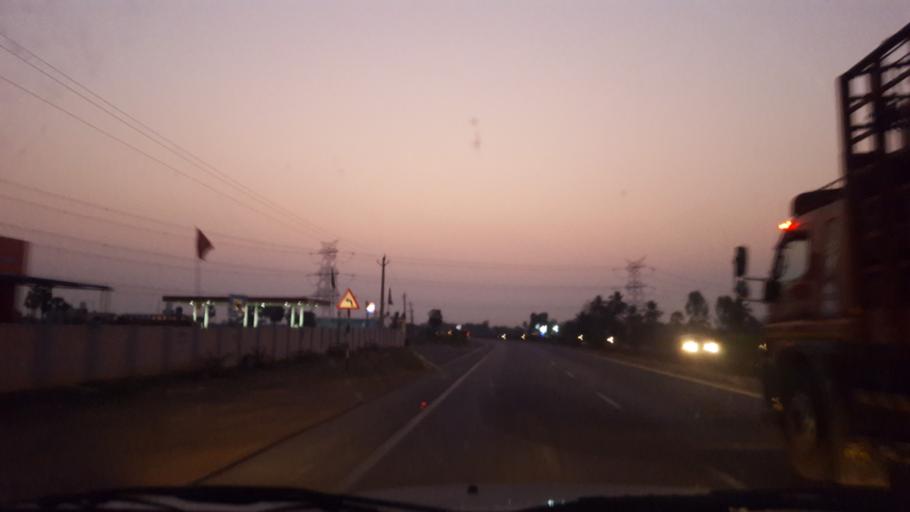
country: IN
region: Andhra Pradesh
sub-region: East Godavari
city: Peddapuram
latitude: 17.1324
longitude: 81.9499
